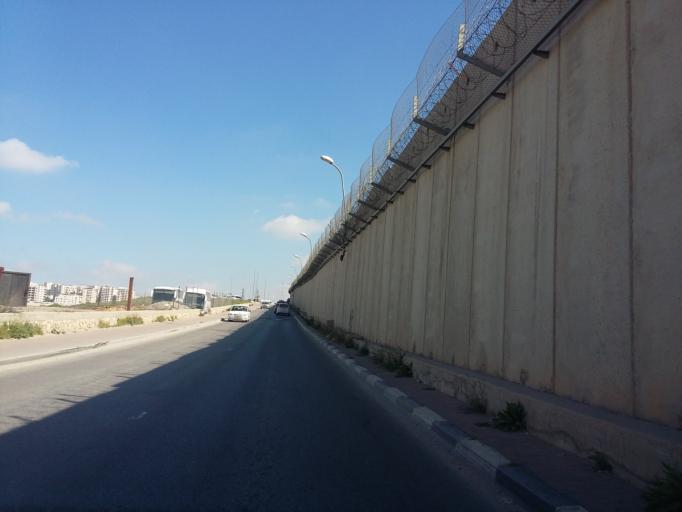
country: PS
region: West Bank
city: Ar Ram wa Dahiyat al Barid
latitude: 31.8574
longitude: 35.2251
